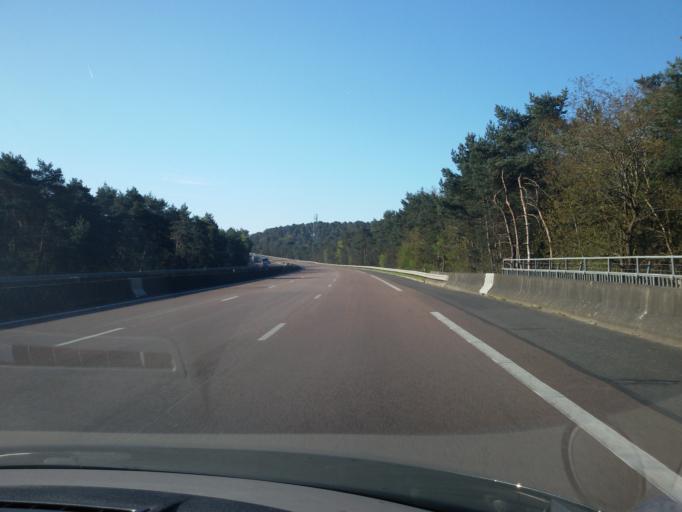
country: FR
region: Ile-de-France
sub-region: Departement de Seine-et-Marne
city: Arbonne-la-Foret
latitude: 48.3940
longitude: 2.5544
